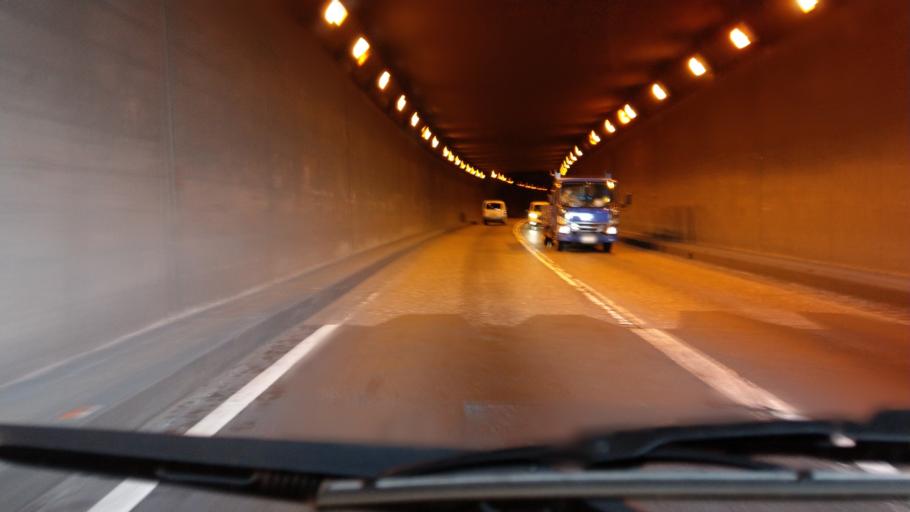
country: JP
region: Nagano
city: Ueda
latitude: 36.4011
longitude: 138.2900
